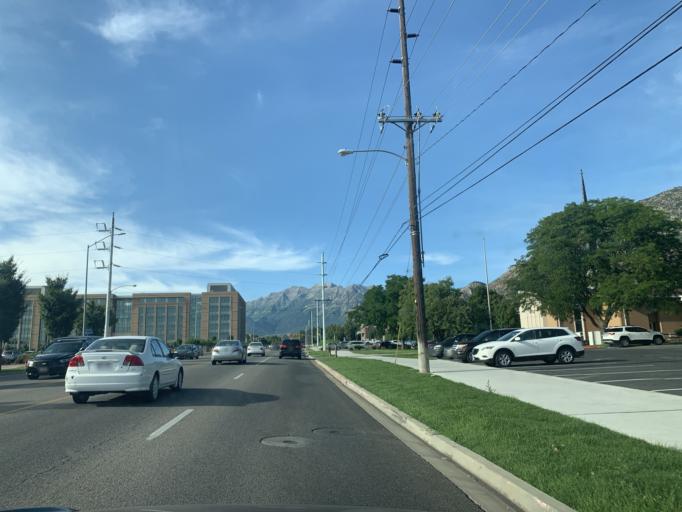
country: US
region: Utah
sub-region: Utah County
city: Provo
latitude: 40.2543
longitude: -111.6431
